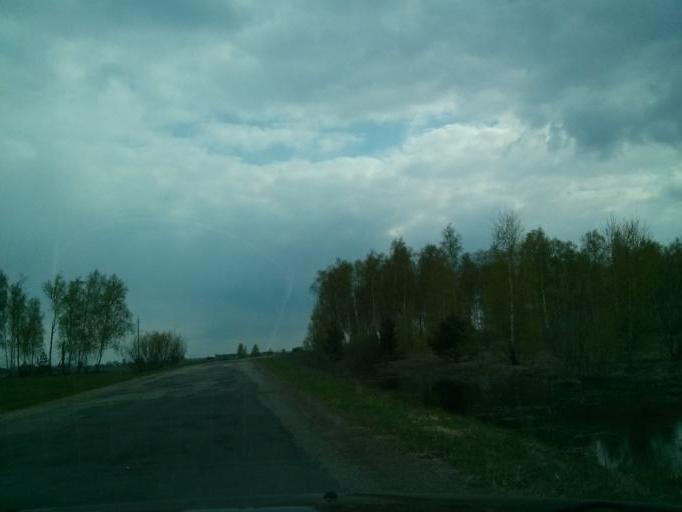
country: RU
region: Vladimir
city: Melenki
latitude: 55.3262
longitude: 41.7768
